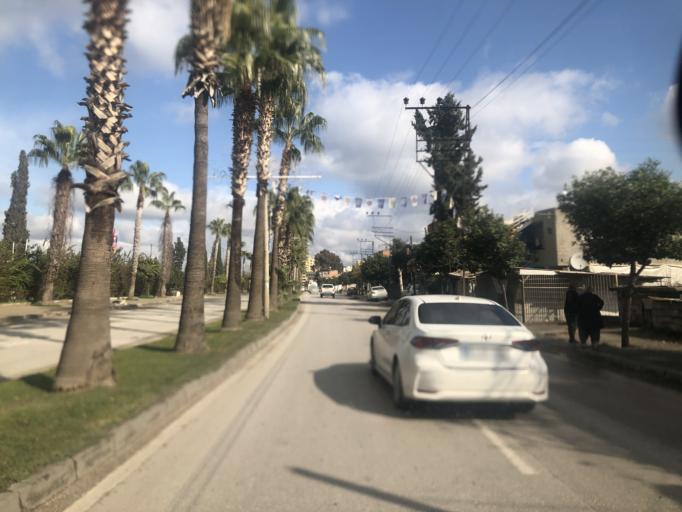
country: TR
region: Adana
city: Adana
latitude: 36.9944
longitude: 35.3405
